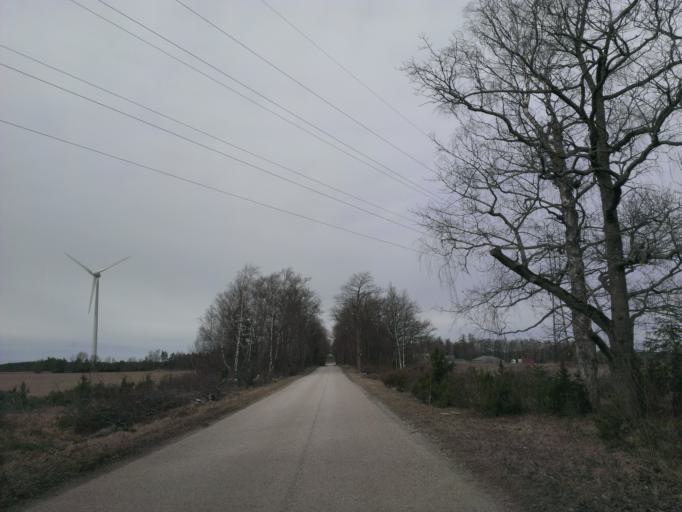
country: EE
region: Laeaene
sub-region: Lihula vald
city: Lihula
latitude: 58.5858
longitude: 23.5372
